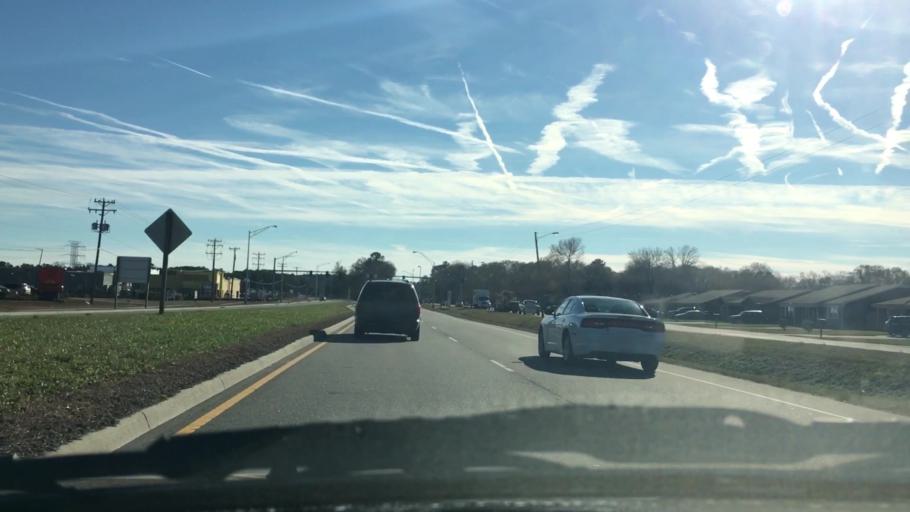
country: US
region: Virginia
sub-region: City of Portsmouth
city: Portsmouth Heights
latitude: 36.8760
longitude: -76.4232
